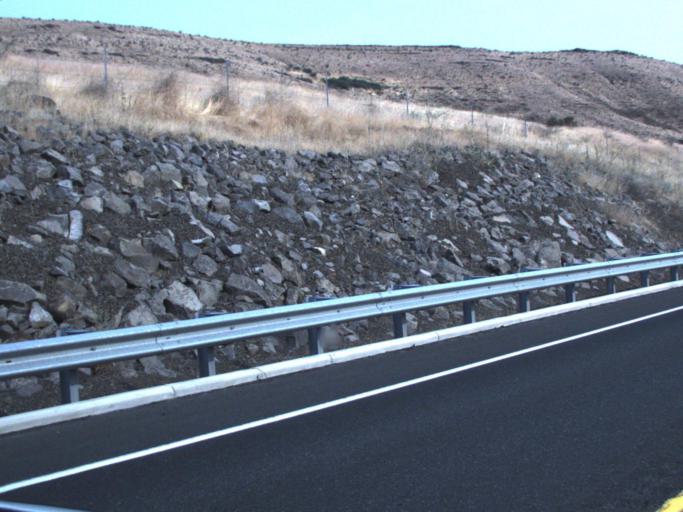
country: US
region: Washington
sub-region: Yakima County
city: Toppenish
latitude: 46.1943
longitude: -120.4896
